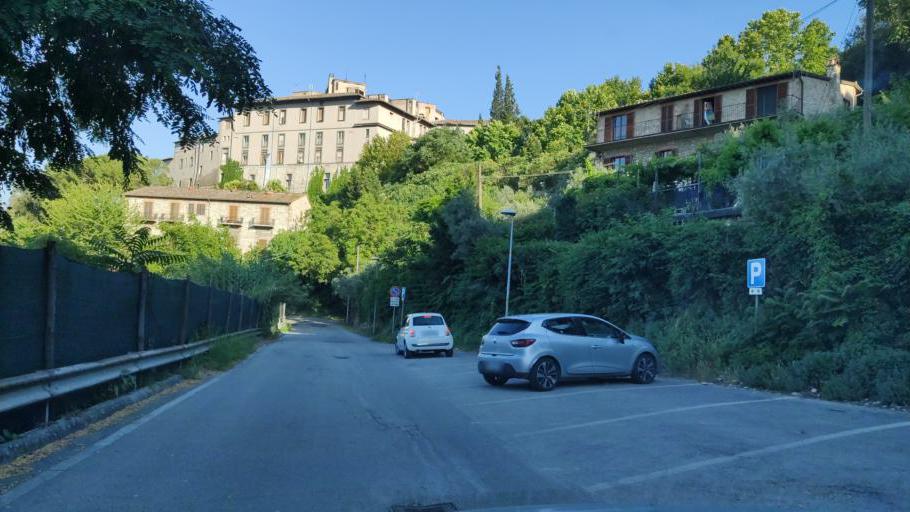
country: IT
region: Umbria
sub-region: Provincia di Terni
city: Narni
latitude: 42.5179
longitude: 12.5202
